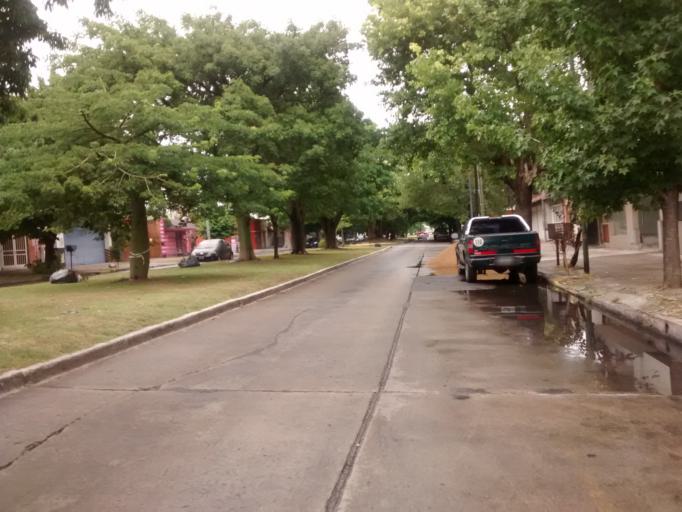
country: AR
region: Buenos Aires
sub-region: Partido de La Plata
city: La Plata
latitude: -34.9139
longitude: -57.9783
